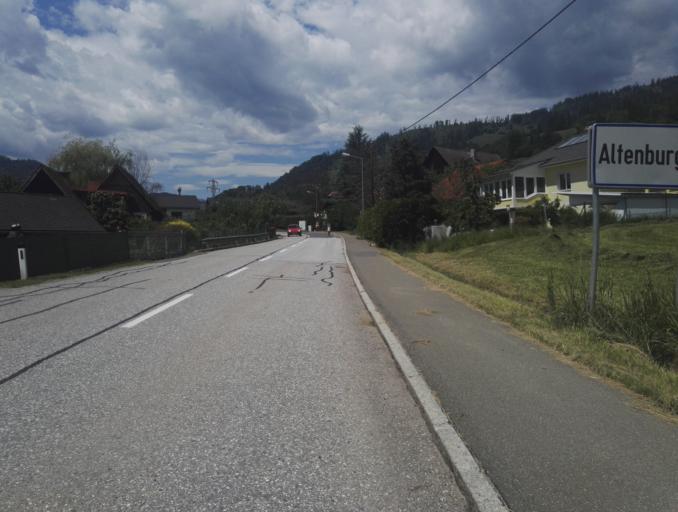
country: AT
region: Styria
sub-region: Politischer Bezirk Graz-Umgebung
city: Ubelbach
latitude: 47.2188
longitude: 15.2707
